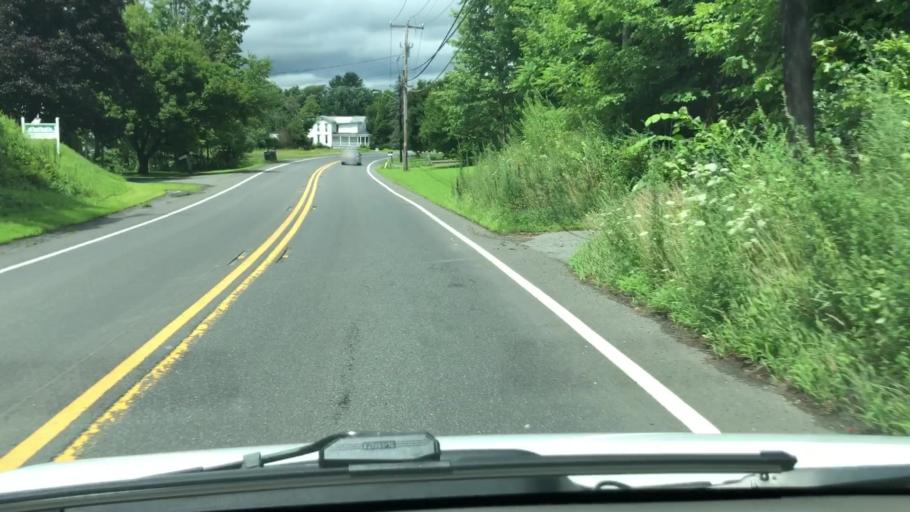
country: US
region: Massachusetts
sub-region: Franklin County
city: South Deerfield
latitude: 42.5178
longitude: -72.6057
